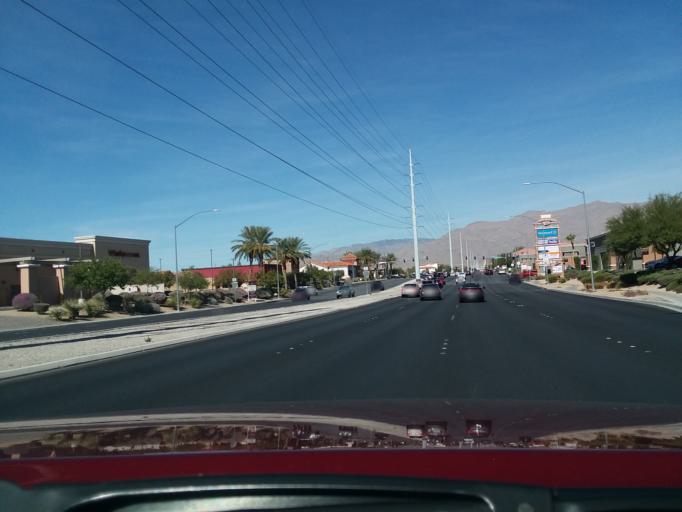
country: US
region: Nevada
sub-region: Clark County
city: North Las Vegas
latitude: 36.2771
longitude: -115.2063
